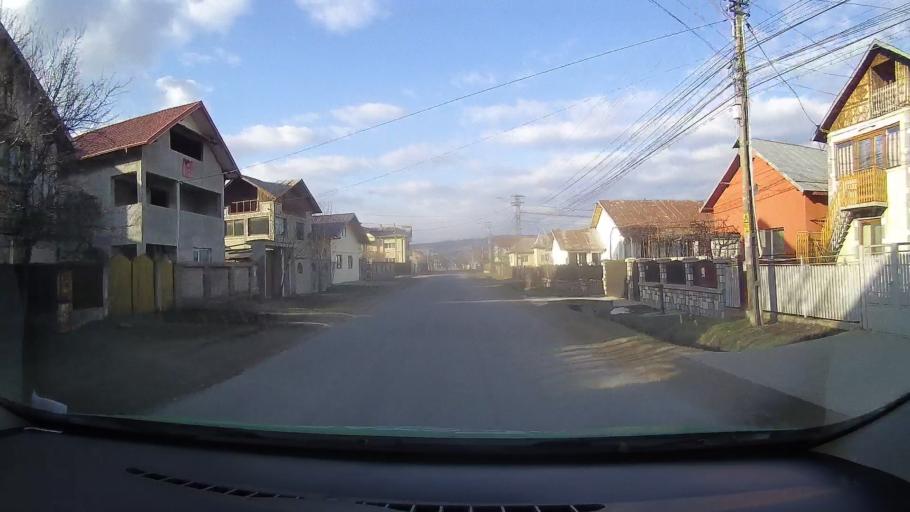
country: RO
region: Dambovita
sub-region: Comuna Ocnita
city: Ocnita
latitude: 44.9744
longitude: 25.5562
